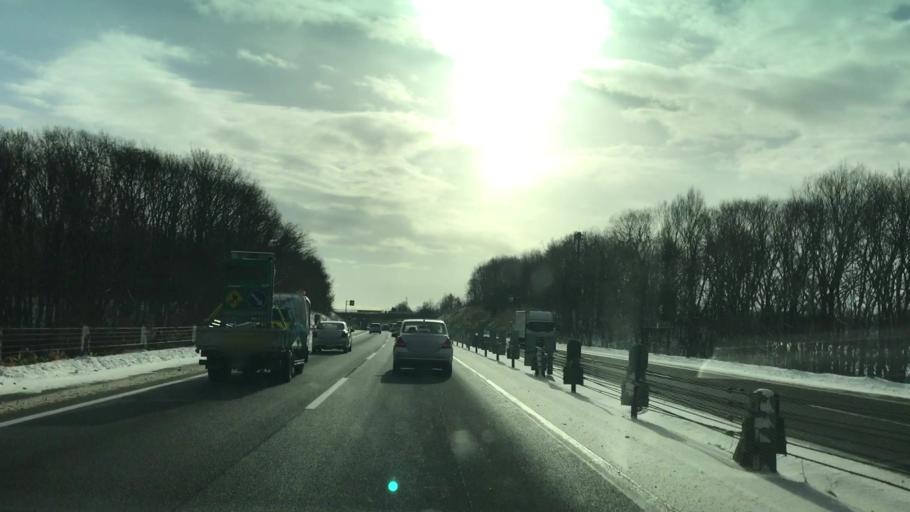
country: JP
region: Hokkaido
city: Kitahiroshima
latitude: 42.9397
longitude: 141.5221
